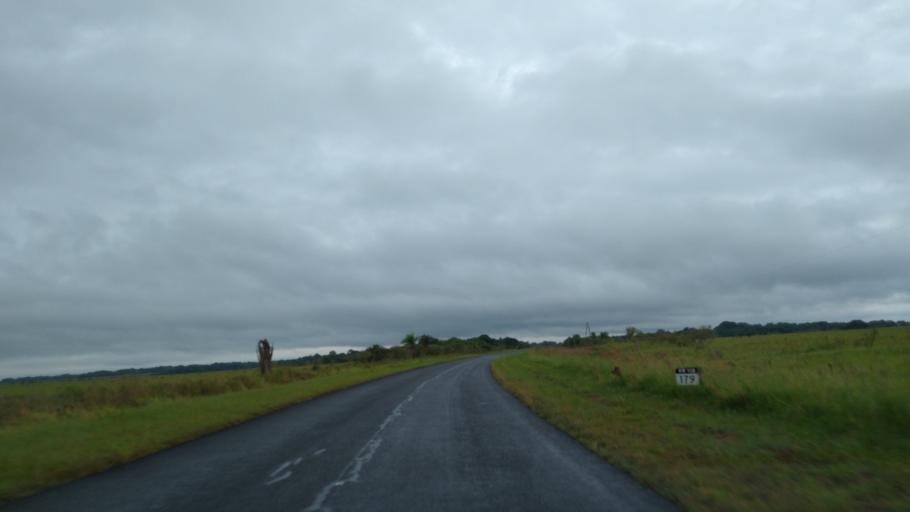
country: AR
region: Corrientes
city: Loreto
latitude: -27.6885
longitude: -57.2143
